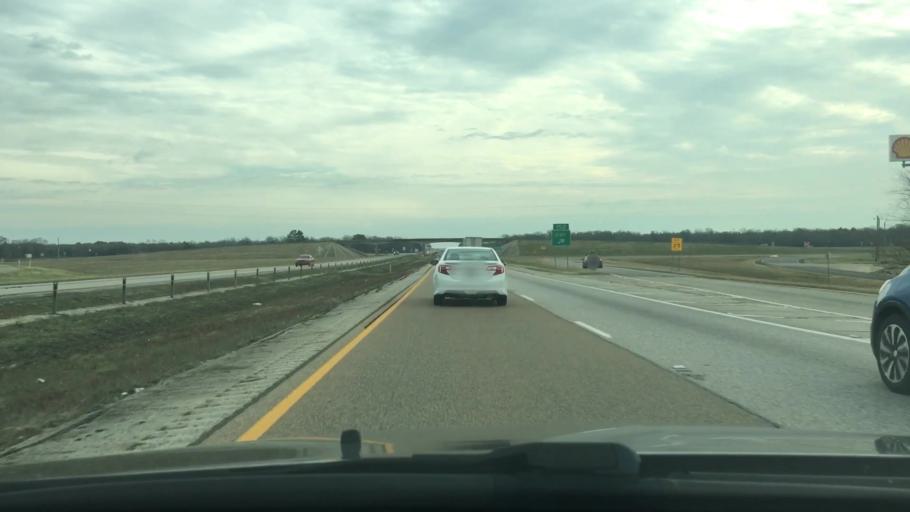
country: US
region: Texas
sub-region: Madison County
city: Madisonville
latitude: 31.0954
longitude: -95.9621
